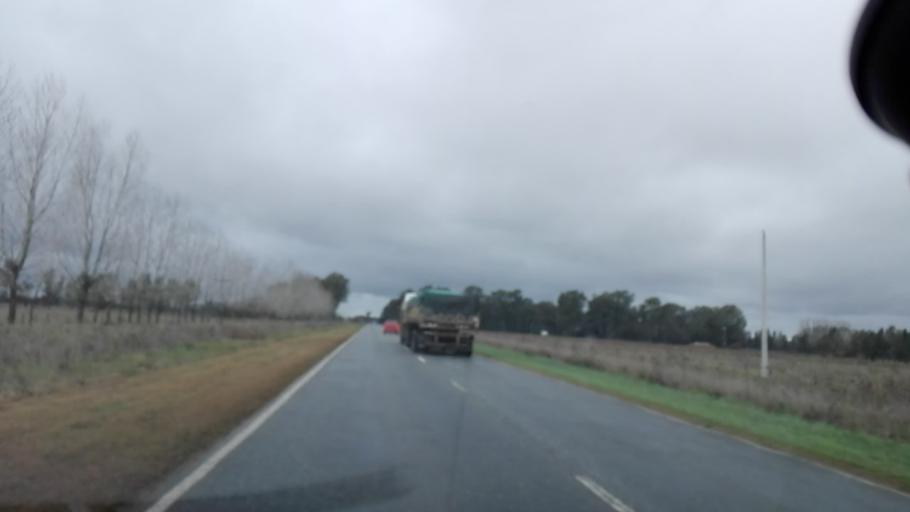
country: AR
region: Buenos Aires
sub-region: Partido de Brandsen
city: Brandsen
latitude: -35.1775
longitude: -58.2941
